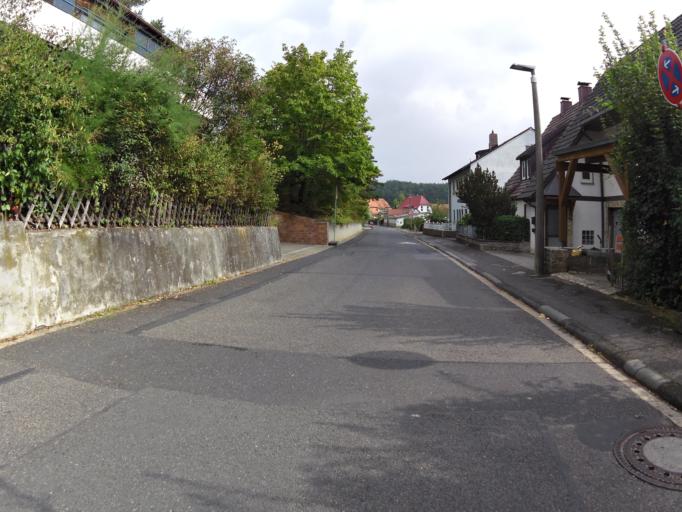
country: DE
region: Bavaria
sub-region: Regierungsbezirk Unterfranken
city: Guntersleben
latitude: 49.8711
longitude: 9.9014
